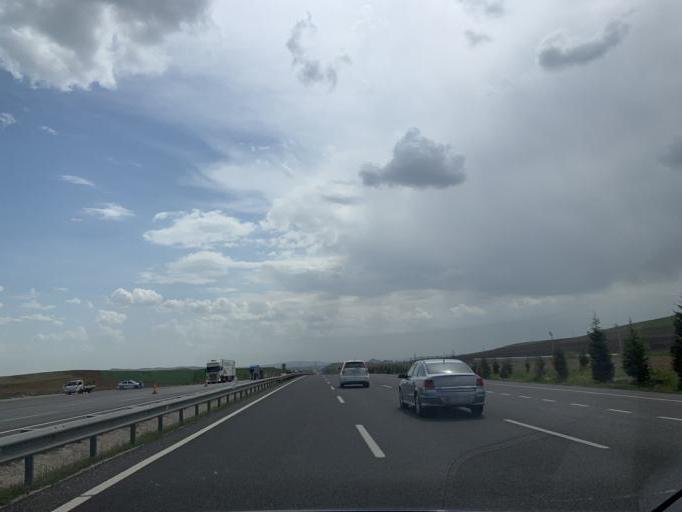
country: TR
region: Ankara
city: Polatli
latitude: 39.6153
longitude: 32.1866
